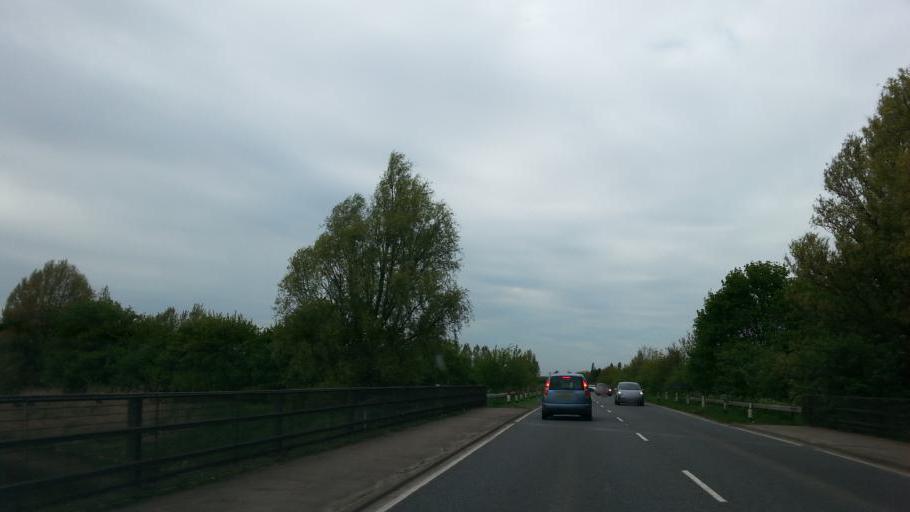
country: GB
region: England
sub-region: Cambridgeshire
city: March
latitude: 52.5531
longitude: 0.0679
